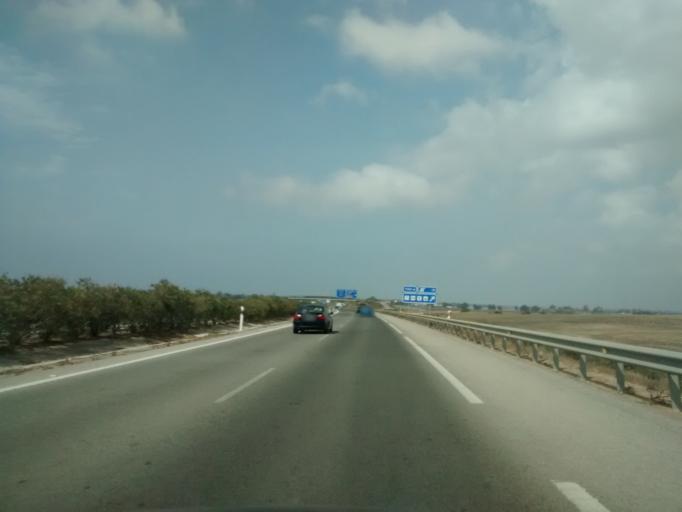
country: ES
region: Andalusia
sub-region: Provincia de Cadiz
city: Conil de la Frontera
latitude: 36.3558
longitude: -6.0890
